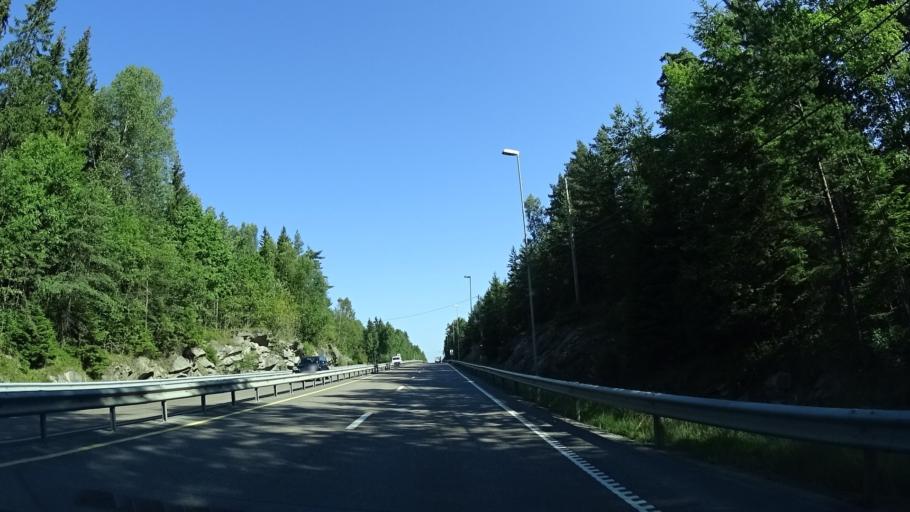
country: NO
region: Akershus
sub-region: Oppegard
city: Kolbotn
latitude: 59.7911
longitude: 10.7607
